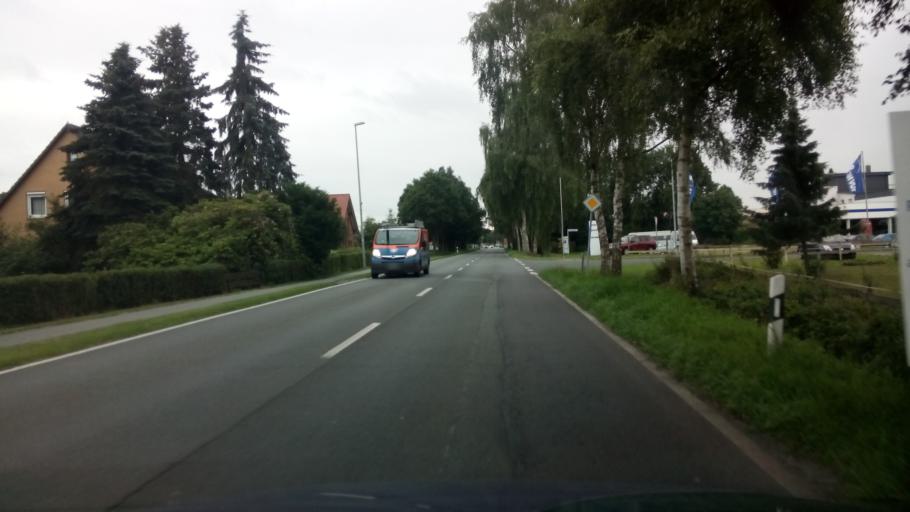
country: DE
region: Lower Saxony
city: Grasberg
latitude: 53.1878
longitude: 8.9807
